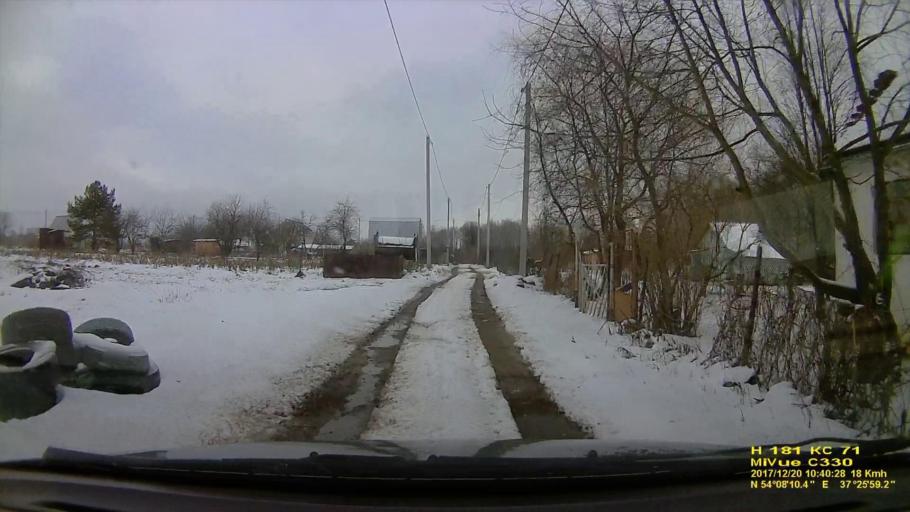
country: RU
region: Tula
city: Kosaya Gora
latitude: 54.1362
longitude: 37.4333
